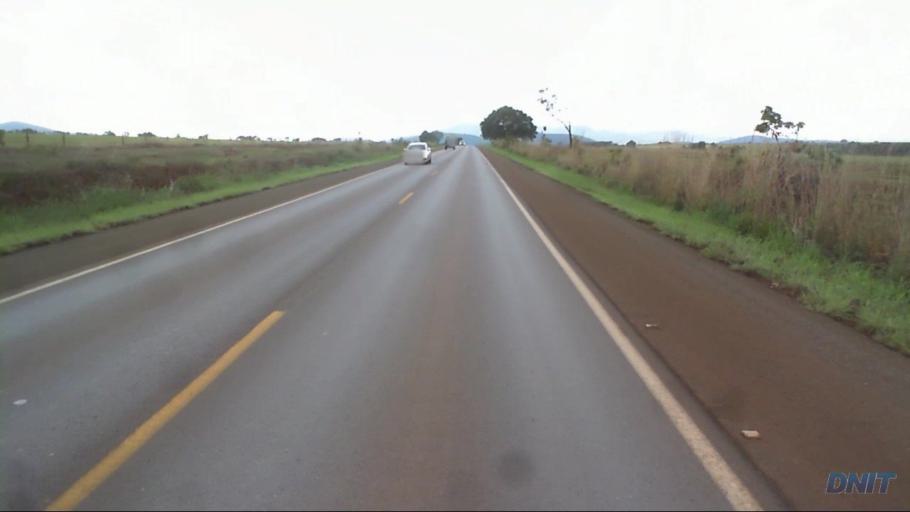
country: BR
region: Goias
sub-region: Barro Alto
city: Barro Alto
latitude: -14.8476
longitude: -49.0269
